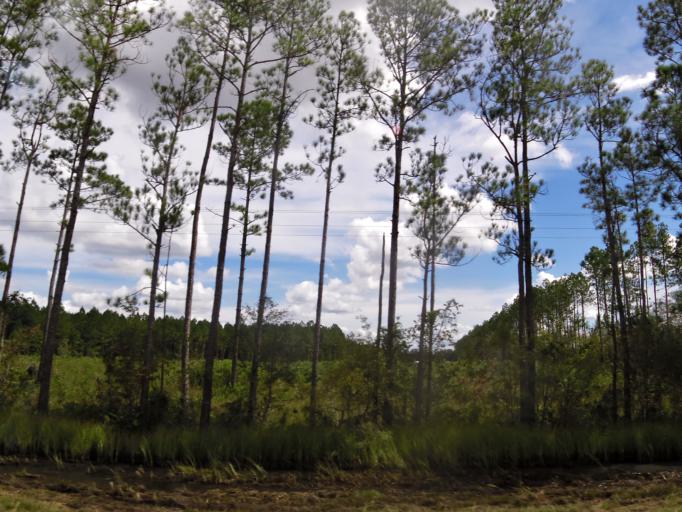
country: US
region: Georgia
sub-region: Brantley County
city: Nahunta
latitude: 31.1419
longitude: -81.9936
